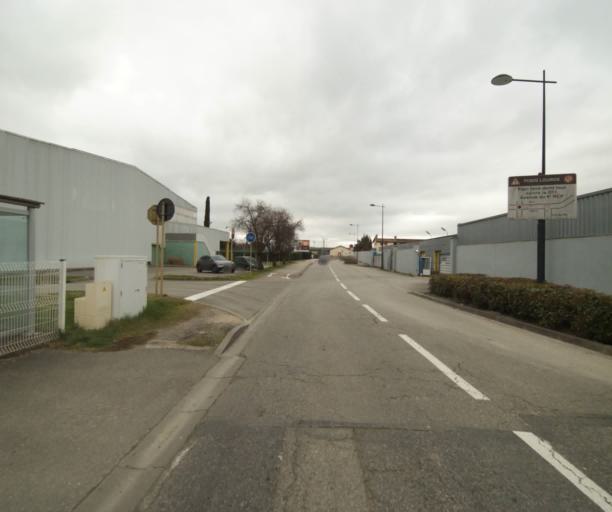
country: FR
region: Midi-Pyrenees
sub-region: Departement de l'Ariege
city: Pamiers
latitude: 43.1200
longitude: 1.6217
